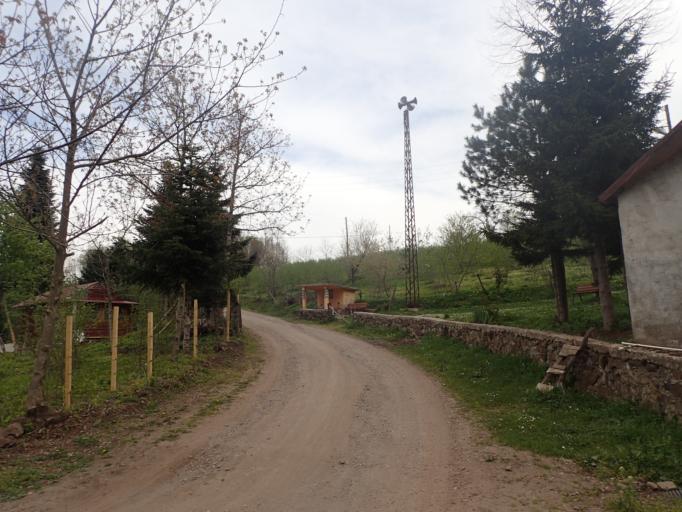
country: TR
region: Ordu
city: Aybasti
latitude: 40.7208
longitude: 37.2923
